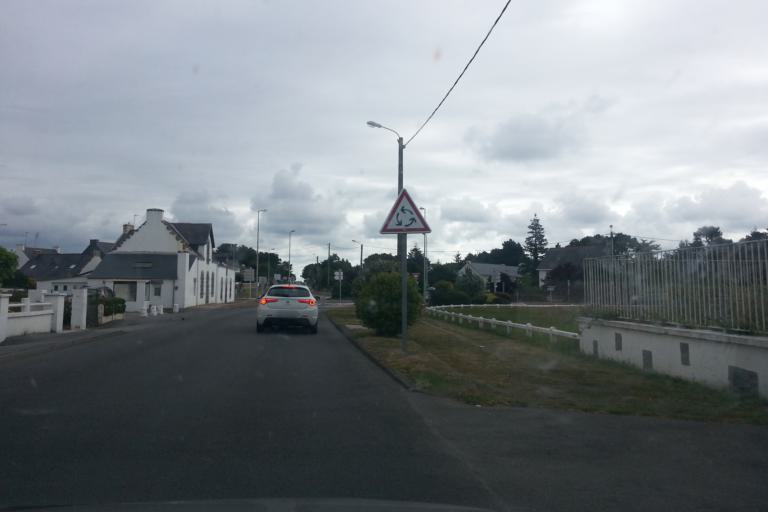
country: FR
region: Brittany
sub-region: Departement du Morbihan
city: Belz
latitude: 47.6655
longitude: -3.1800
